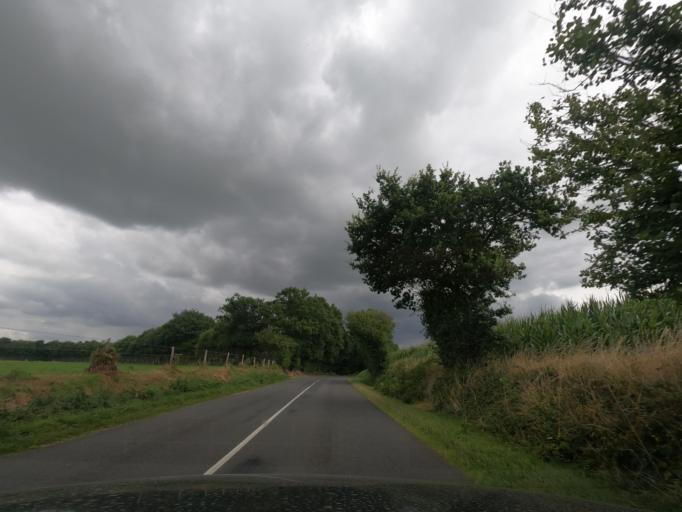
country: FR
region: Lower Normandy
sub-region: Departement de l'Orne
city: Briouze
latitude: 48.6910
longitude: -0.4041
